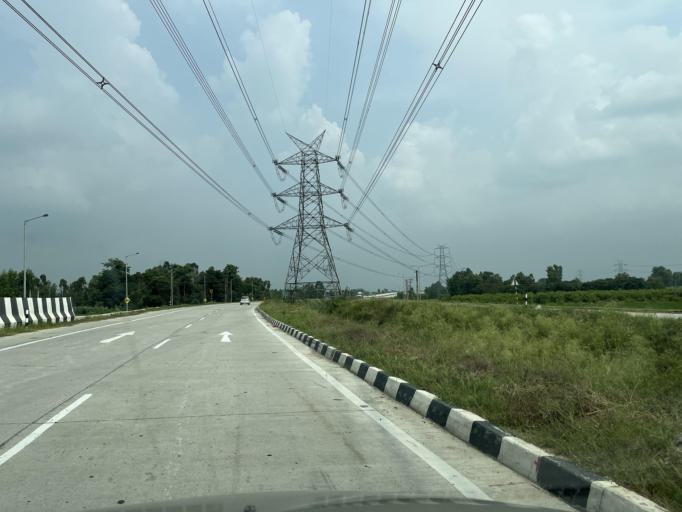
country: IN
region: Uttarakhand
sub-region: Udham Singh Nagar
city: Jaspur
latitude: 29.2984
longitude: 78.8347
